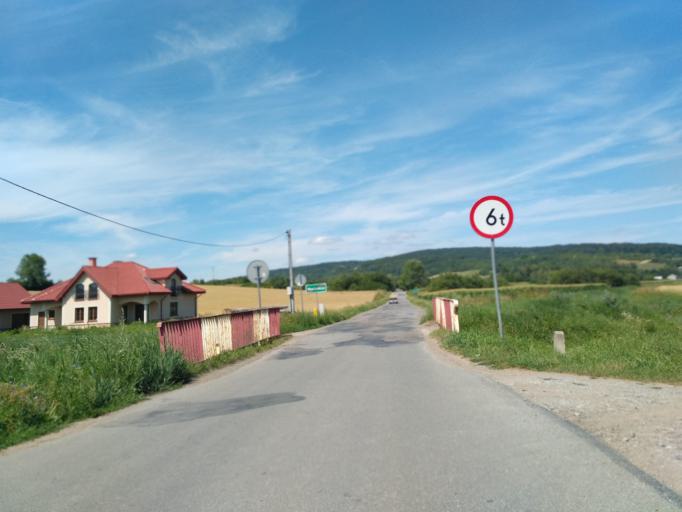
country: PL
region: Subcarpathian Voivodeship
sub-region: Powiat sanocki
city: Nowosielce-Gniewosz
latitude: 49.5493
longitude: 22.1074
